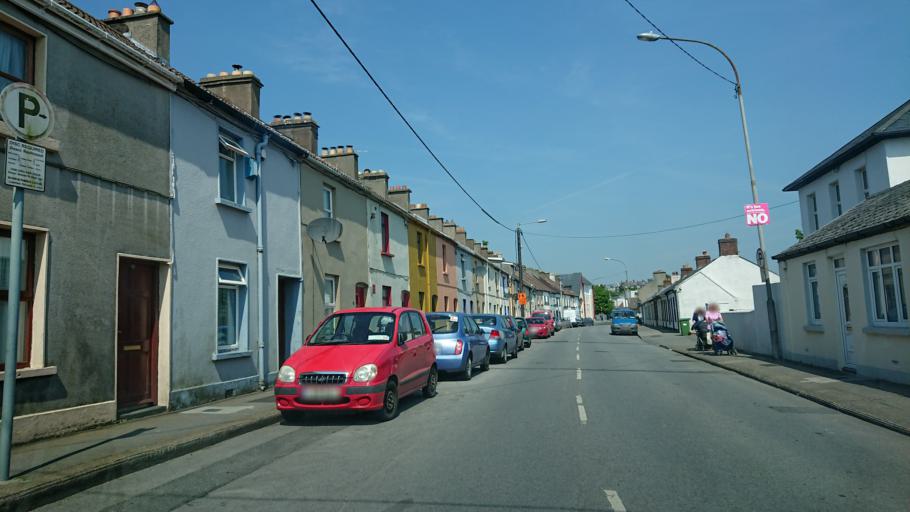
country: IE
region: Munster
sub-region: Waterford
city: Waterford
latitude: 52.2519
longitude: -7.1121
